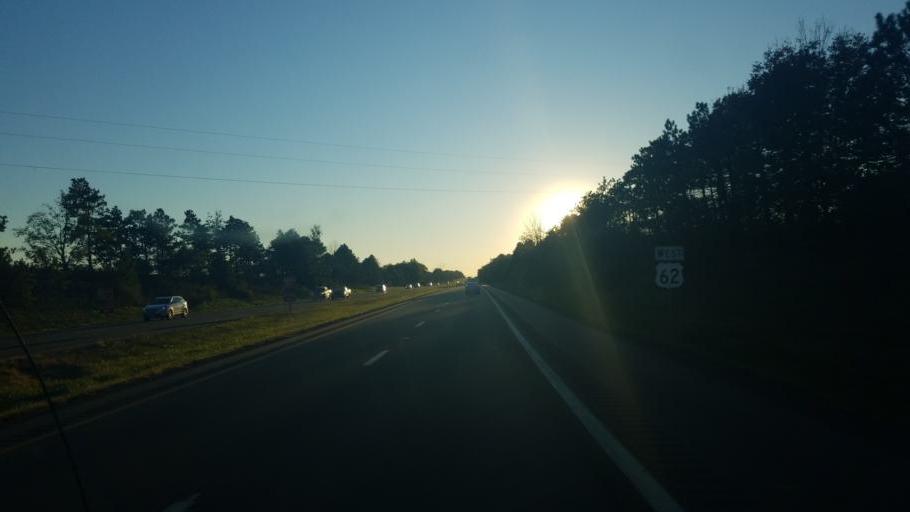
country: US
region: Ohio
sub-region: Stark County
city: Louisville
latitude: 40.8890
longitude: -81.1985
